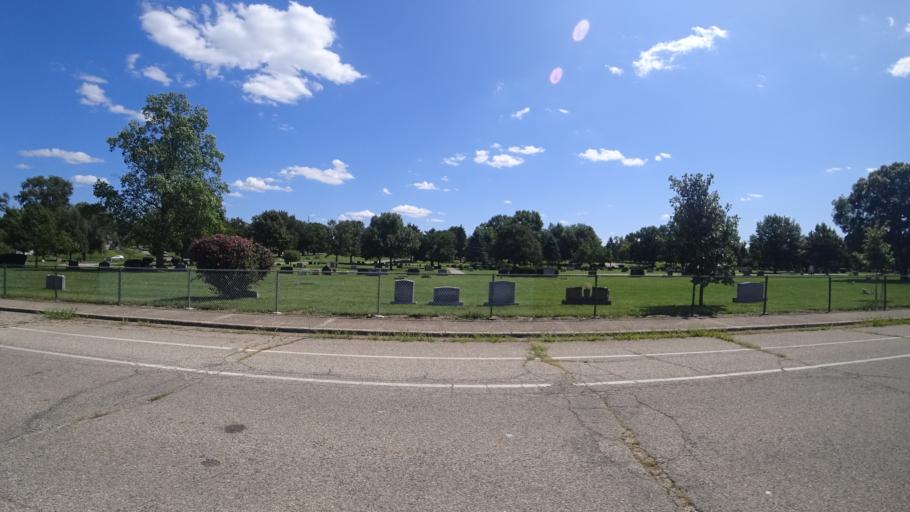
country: US
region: Ohio
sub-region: Butler County
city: Hamilton
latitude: 39.4090
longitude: -84.5399
